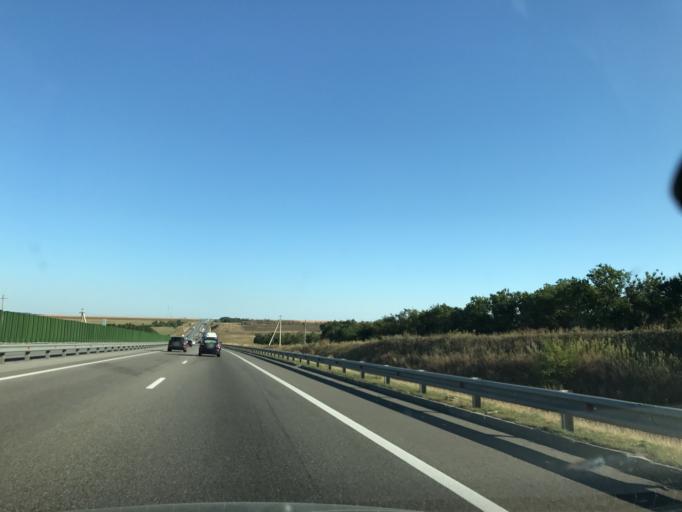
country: RU
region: Rostov
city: Glubokiy
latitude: 48.5990
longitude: 40.3538
